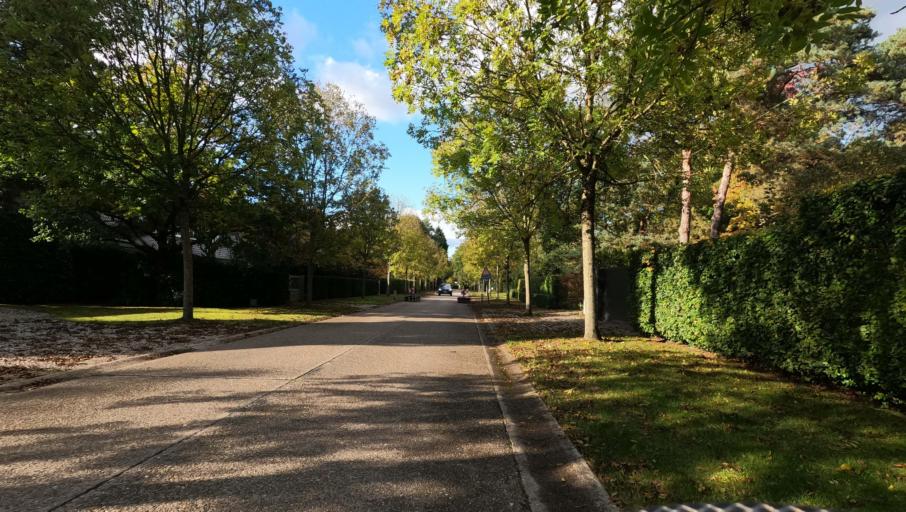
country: BE
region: Flanders
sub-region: Provincie Antwerpen
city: Schilde
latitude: 51.2394
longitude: 4.5725
